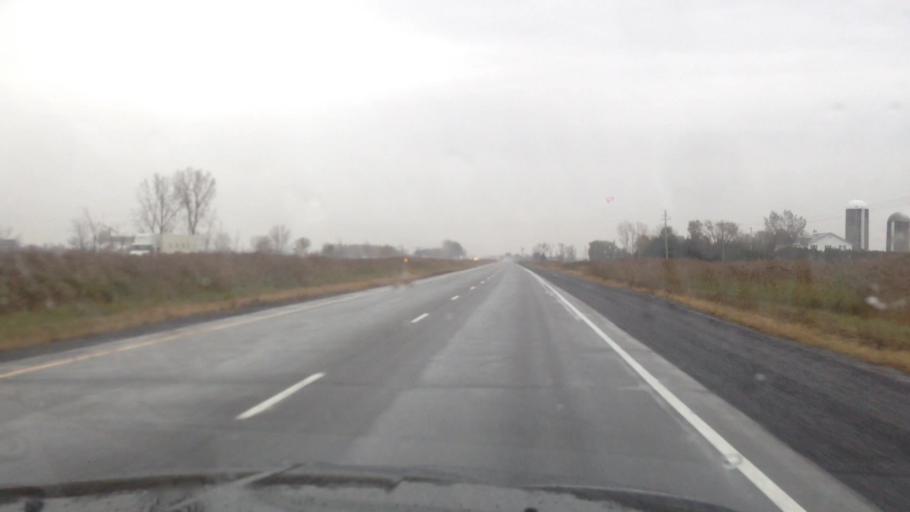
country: CA
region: Ontario
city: Casselman
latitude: 45.3075
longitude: -75.0493
